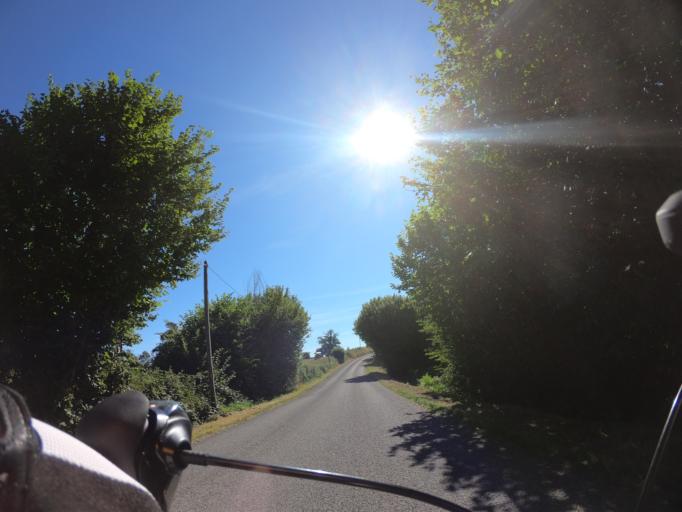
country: FR
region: Pays de la Loire
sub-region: Departement de la Mayenne
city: Pre-en-Pail
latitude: 48.5561
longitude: -0.1202
